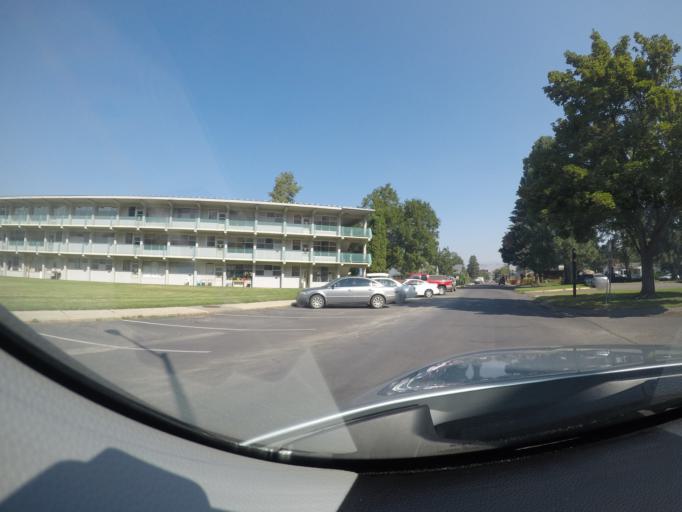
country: US
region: Montana
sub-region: Missoula County
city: Missoula
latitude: 46.8527
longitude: -113.9854
